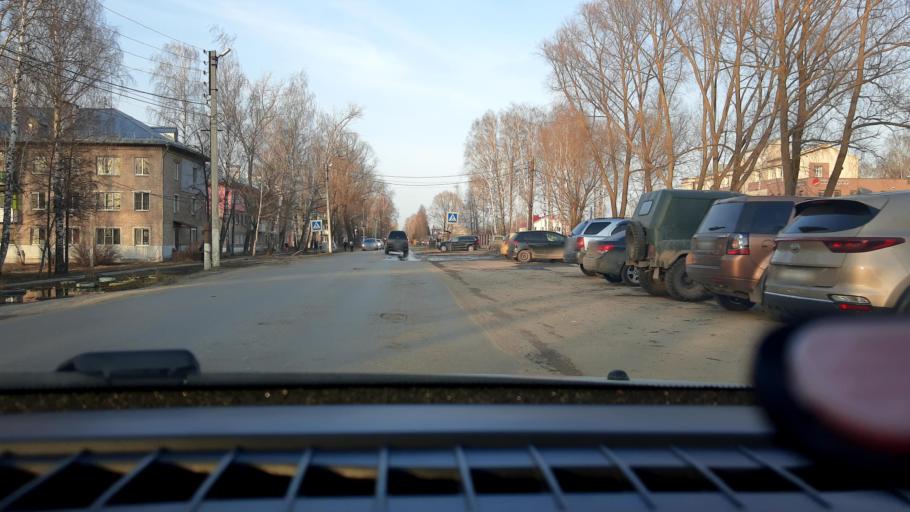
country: RU
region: Nizjnij Novgorod
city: Bogorodsk
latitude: 56.1035
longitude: 43.4842
